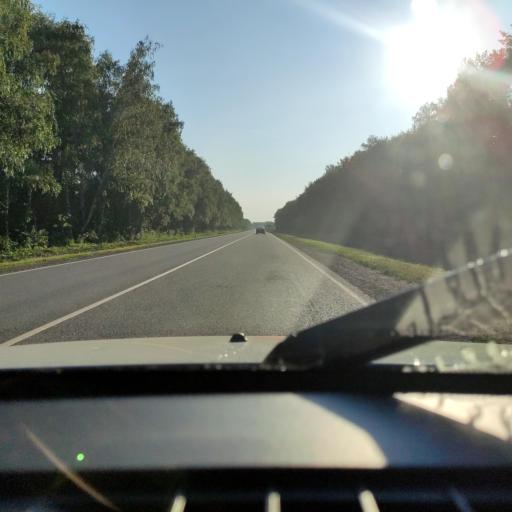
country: RU
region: Voronezj
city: Kashirskoye
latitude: 51.4590
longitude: 39.7919
